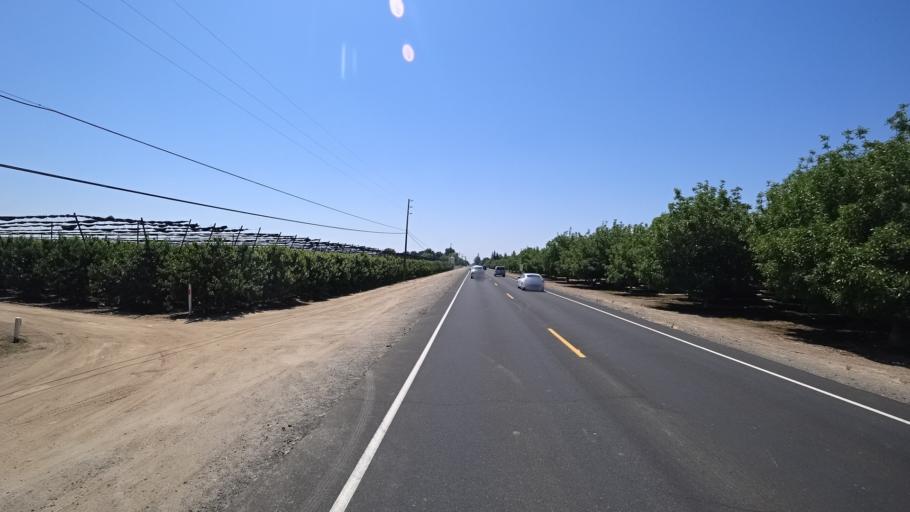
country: US
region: California
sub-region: Kings County
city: Lucerne
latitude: 36.3754
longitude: -119.6730
